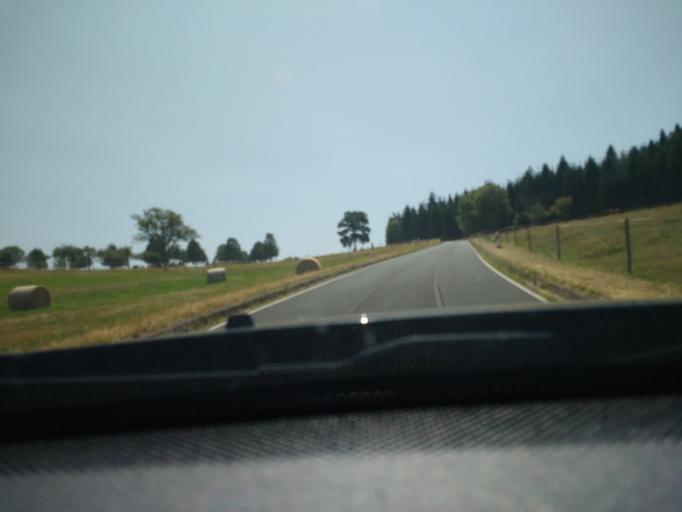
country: DE
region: Rheinland-Pfalz
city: Bettenfeld
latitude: 50.0825
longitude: 6.7516
